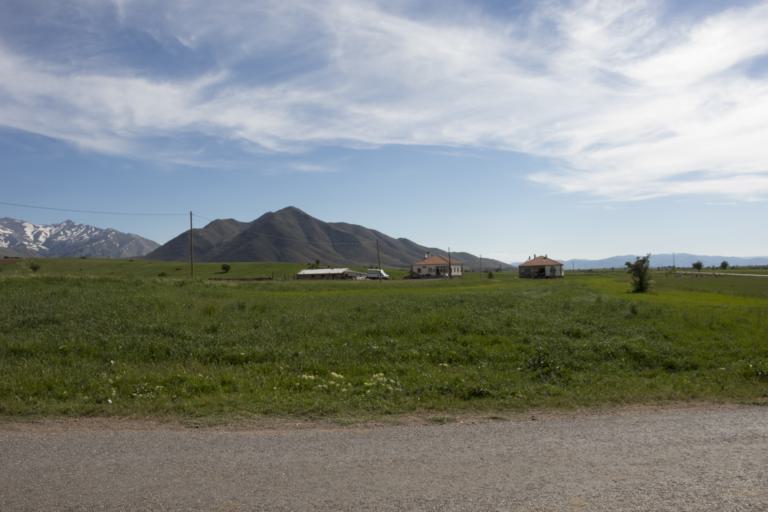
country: TR
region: Kayseri
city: Toklar
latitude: 38.4222
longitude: 36.0898
